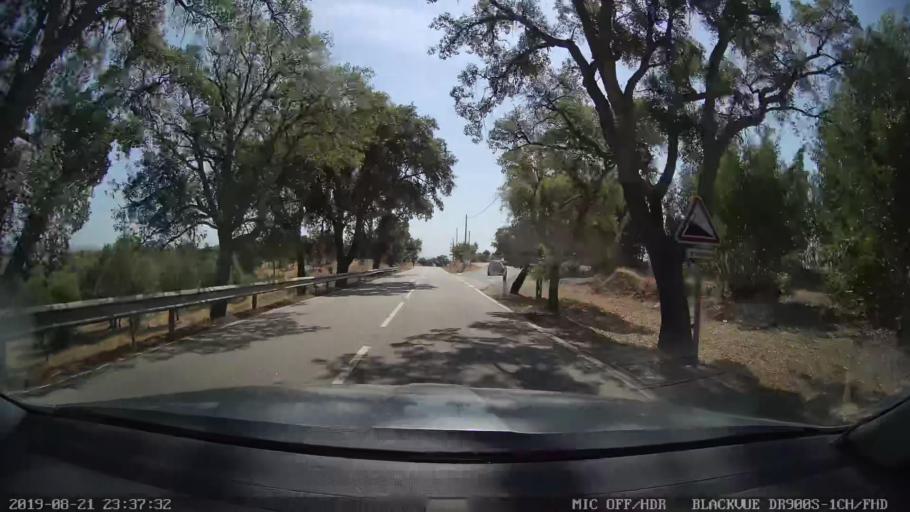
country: PT
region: Guarda
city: Alcains
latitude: 39.8676
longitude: -7.3593
